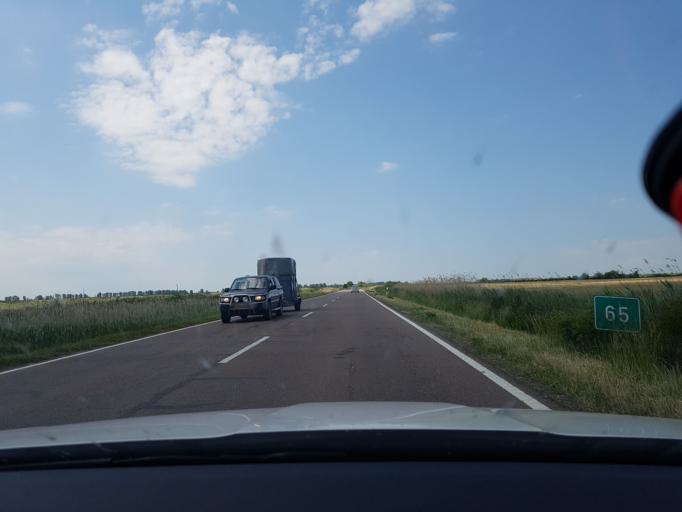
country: HU
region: Hajdu-Bihar
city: Hortobagy
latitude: 47.5901
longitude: 21.0533
